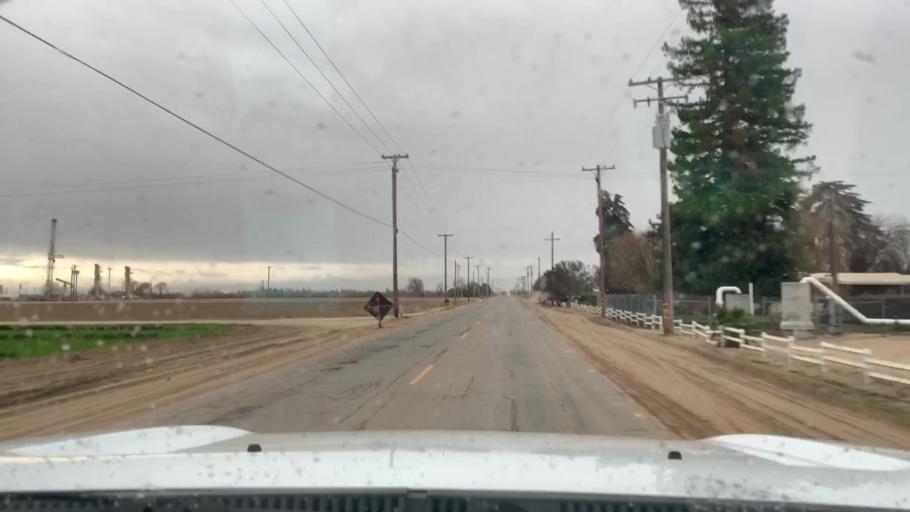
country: US
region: California
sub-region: Kern County
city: Shafter
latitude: 35.5332
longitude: -119.2778
